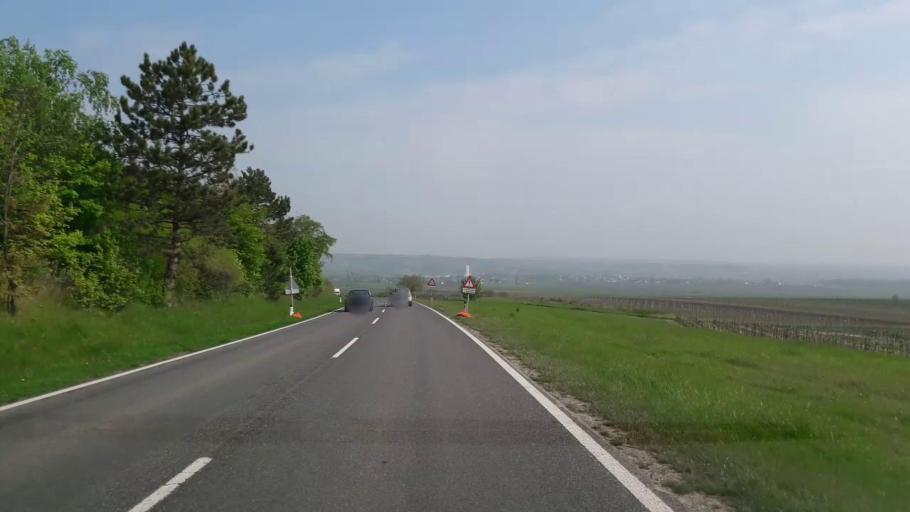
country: AT
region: Lower Austria
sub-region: Politischer Bezirk Hollabrunn
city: Haugsdorf
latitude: 48.6829
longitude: 16.0582
